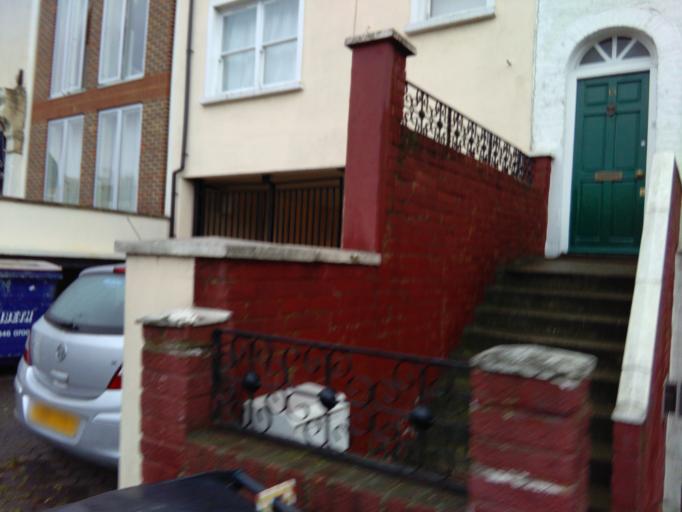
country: GB
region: England
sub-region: Greater London
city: Brixton Hill
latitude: 51.4648
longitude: -0.1293
